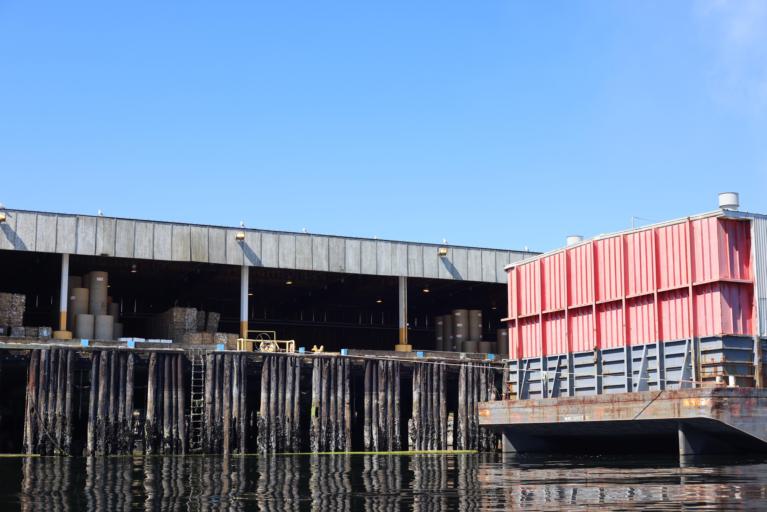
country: CA
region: British Columbia
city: North Cowichan
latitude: 48.8739
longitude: -123.6411
